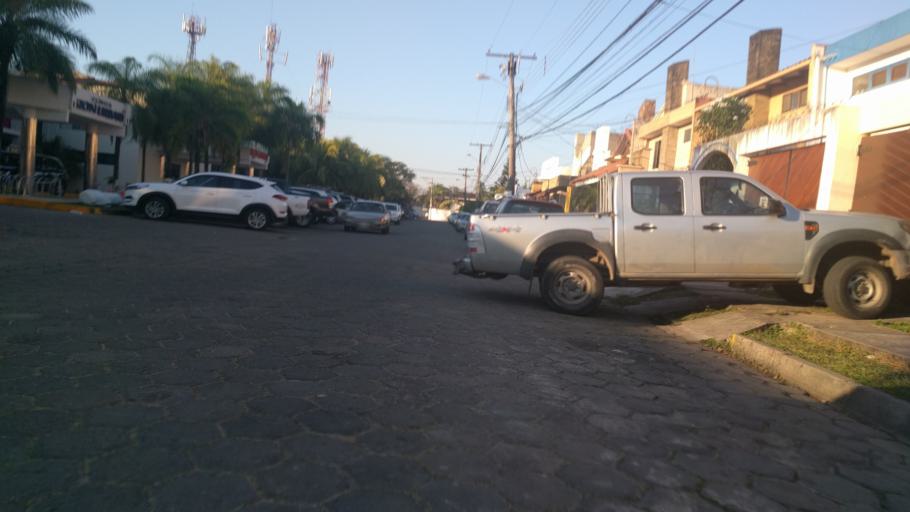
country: BO
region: Santa Cruz
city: Santa Cruz de la Sierra
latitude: -17.7975
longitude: -63.1976
